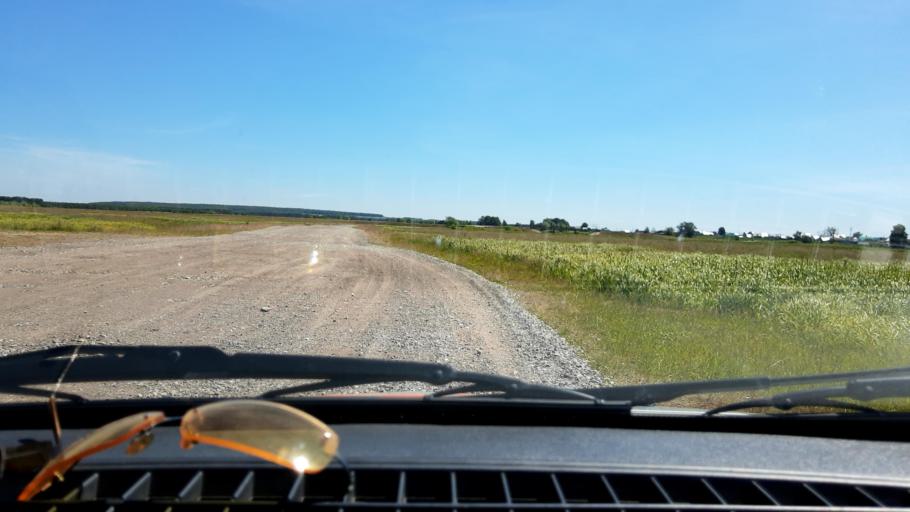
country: RU
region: Bashkortostan
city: Mikhaylovka
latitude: 54.9695
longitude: 55.7961
